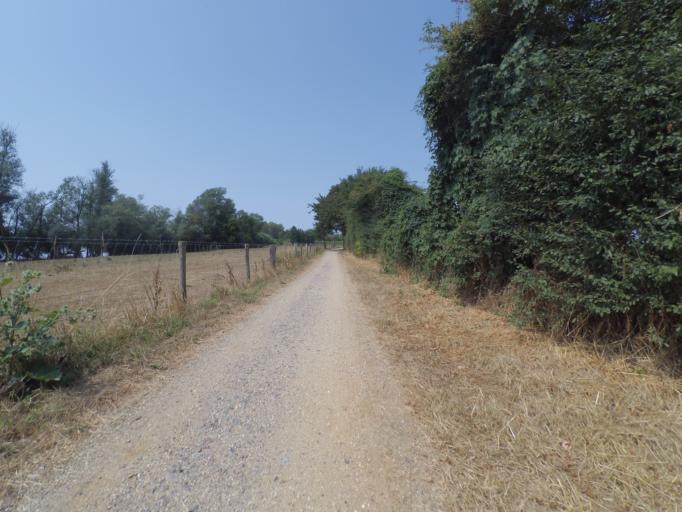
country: DE
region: North Rhine-Westphalia
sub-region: Regierungsbezirk Dusseldorf
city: Mehrhoog
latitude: 51.7629
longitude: 6.4617
